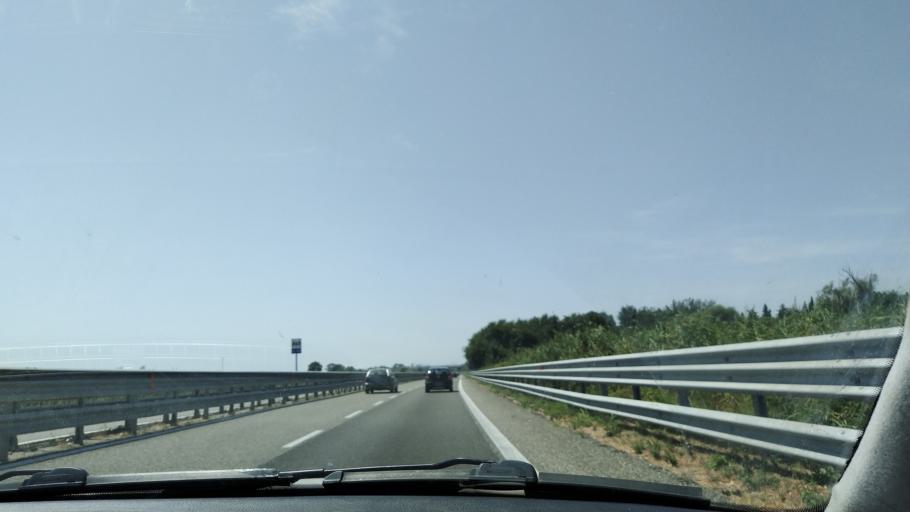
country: IT
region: Basilicate
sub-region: Provincia di Matera
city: Marconia
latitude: 40.3464
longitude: 16.7662
